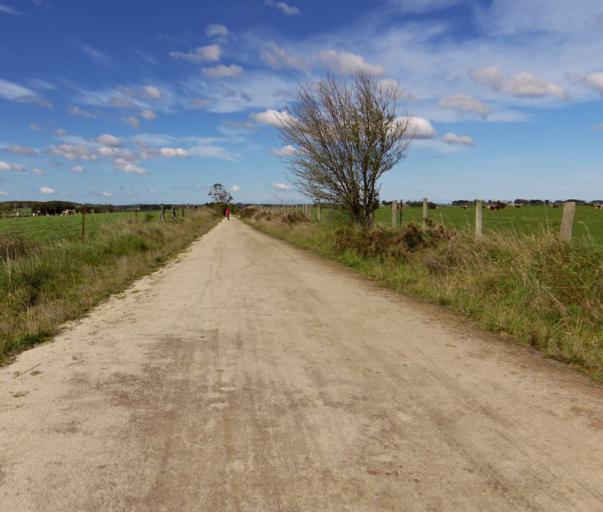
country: AU
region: Victoria
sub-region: Baw Baw
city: Warragul
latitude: -38.5006
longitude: 145.9405
